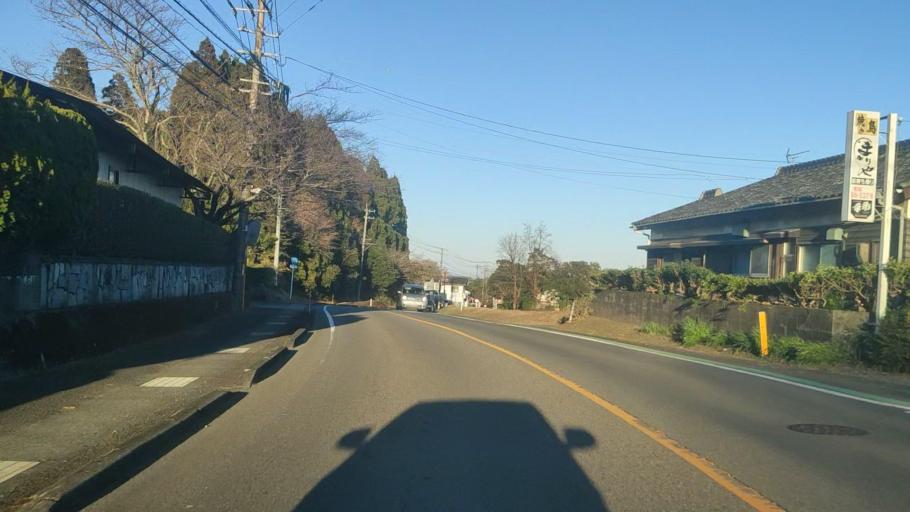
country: JP
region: Miyazaki
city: Miyazaki-shi
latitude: 31.8375
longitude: 131.3329
